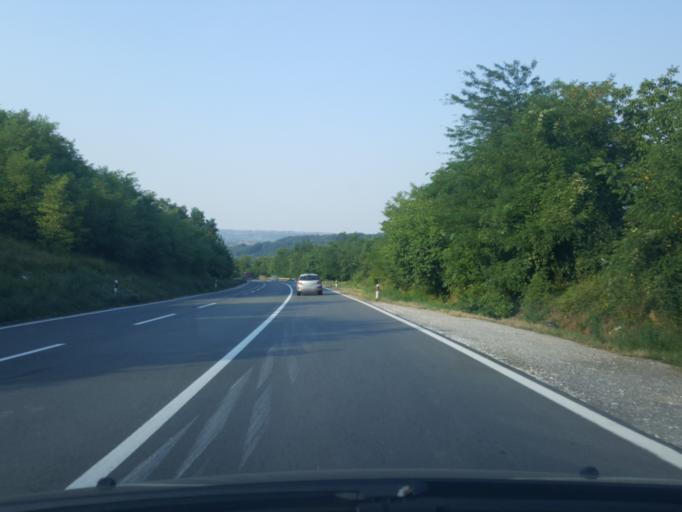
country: RS
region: Central Serbia
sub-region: Belgrade
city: Sopot
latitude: 44.5495
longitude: 20.6633
